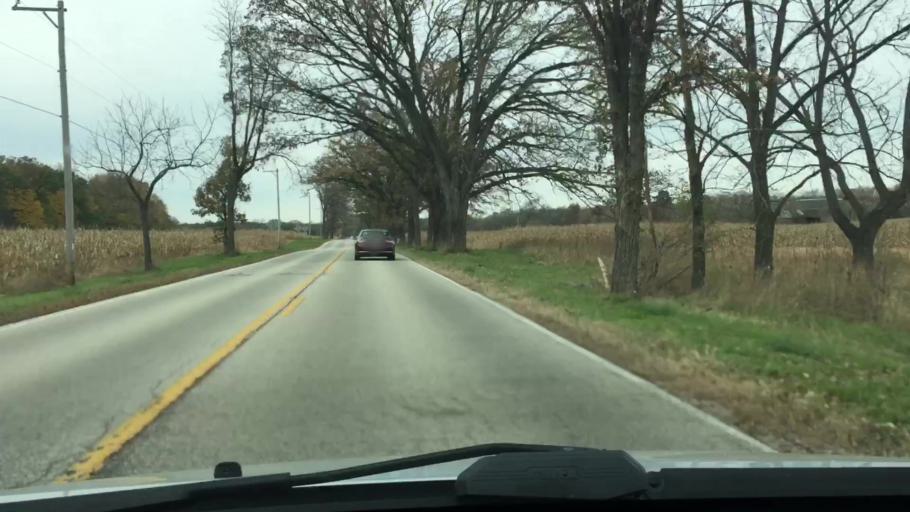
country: US
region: Wisconsin
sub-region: Waukesha County
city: North Prairie
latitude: 42.8940
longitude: -88.3863
